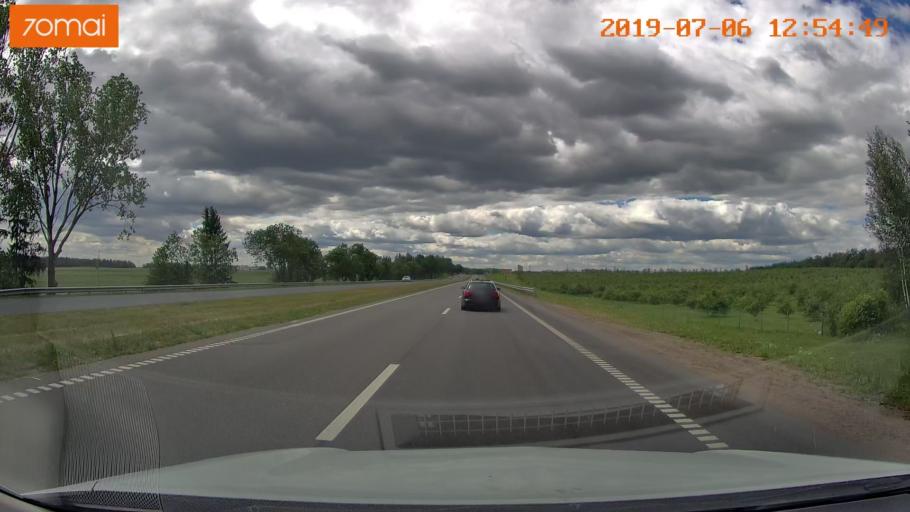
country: BY
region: Minsk
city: Dzyarzhynsk
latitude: 53.6986
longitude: 27.1831
